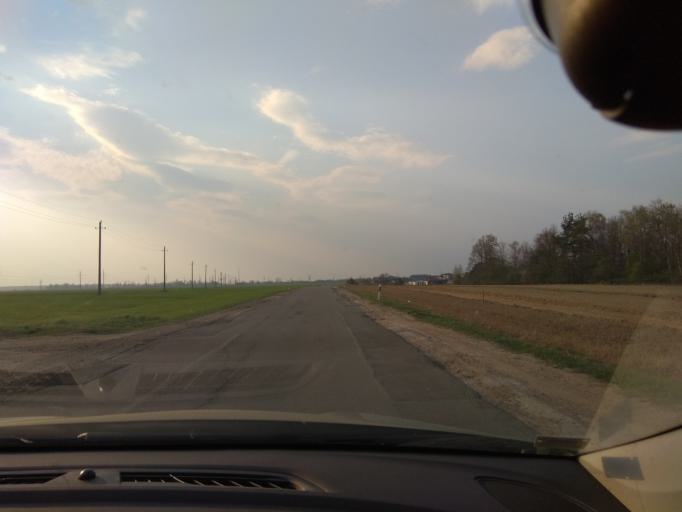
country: LT
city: Baltoji Voke
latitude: 54.6017
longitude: 25.1377
